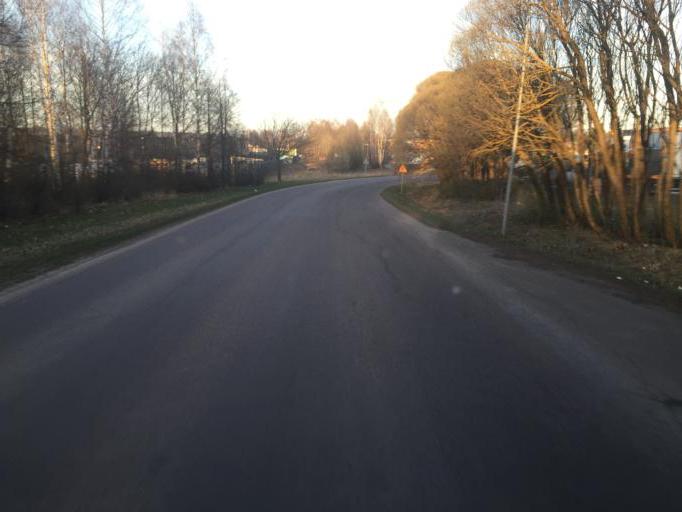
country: SE
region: Dalarna
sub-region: Borlange Kommun
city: Borlaenge
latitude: 60.4687
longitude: 15.4536
